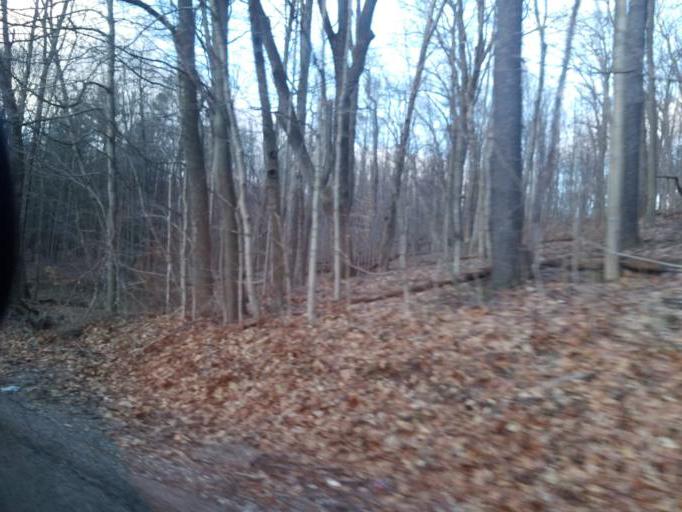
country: US
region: Ohio
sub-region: Sandusky County
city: Bellville
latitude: 40.6238
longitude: -82.3744
